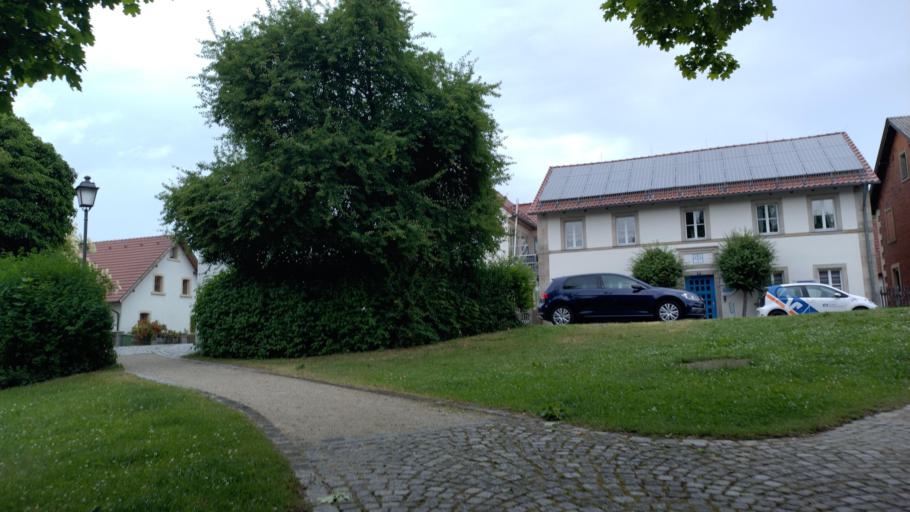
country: DE
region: Bavaria
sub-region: Upper Franconia
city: Bindlach
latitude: 49.9812
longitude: 11.6139
